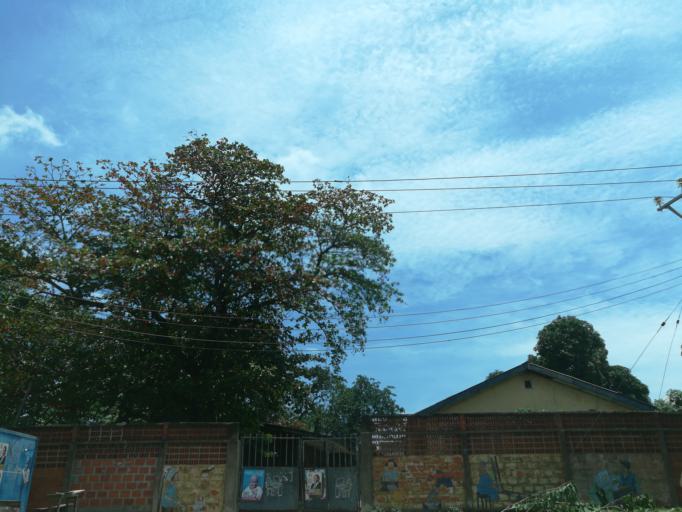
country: NG
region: Lagos
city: Ebute Ikorodu
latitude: 6.6045
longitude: 3.4944
